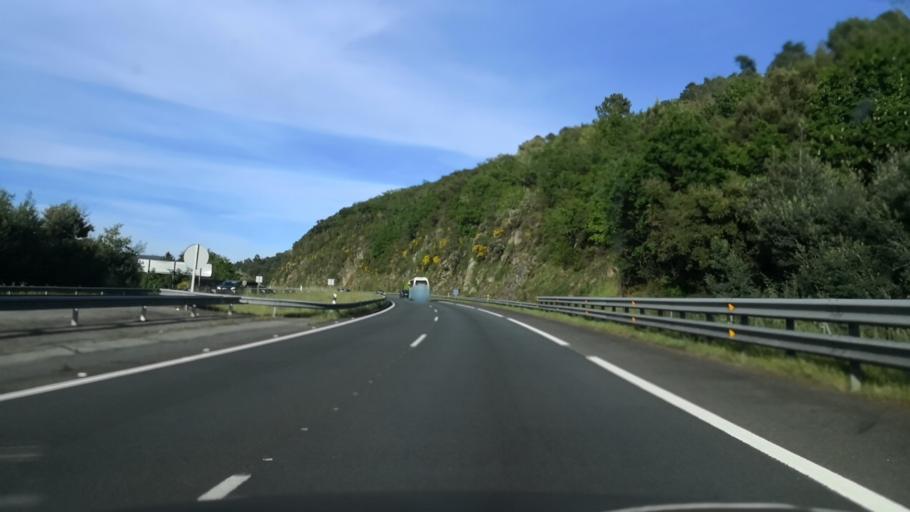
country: ES
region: Galicia
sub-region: Provincia de Ourense
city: Toen
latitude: 42.3306
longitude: -7.9514
